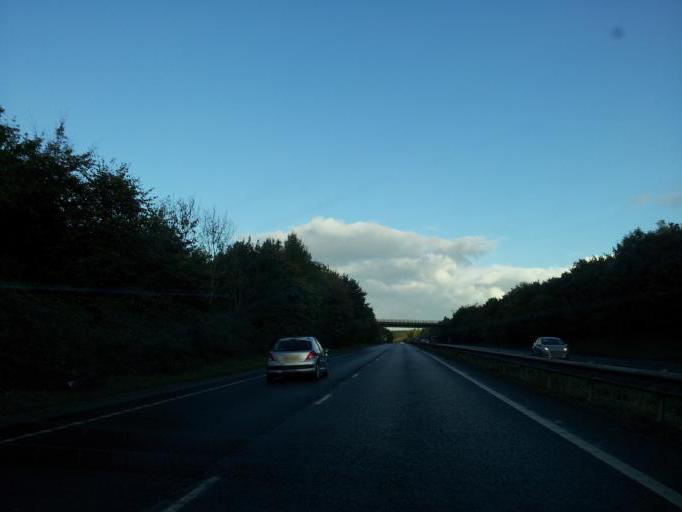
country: GB
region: England
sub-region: Norfolk
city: Bowthorpe
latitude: 52.6147
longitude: 1.2125
